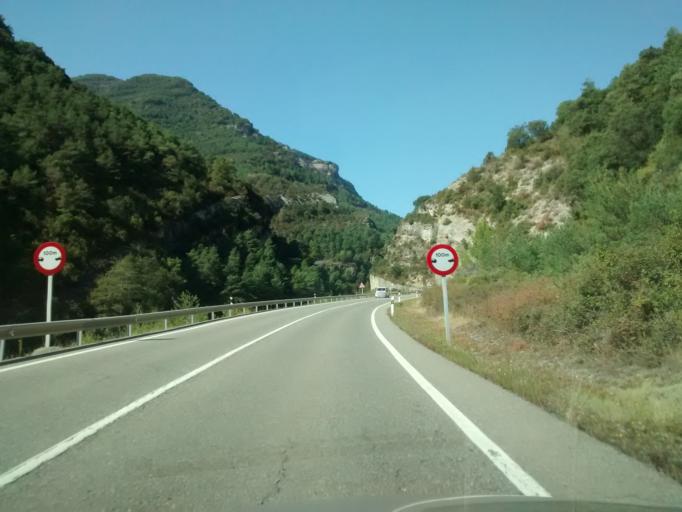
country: ES
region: Aragon
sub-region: Provincia de Huesca
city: Boltana
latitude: 42.4634
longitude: 0.0397
